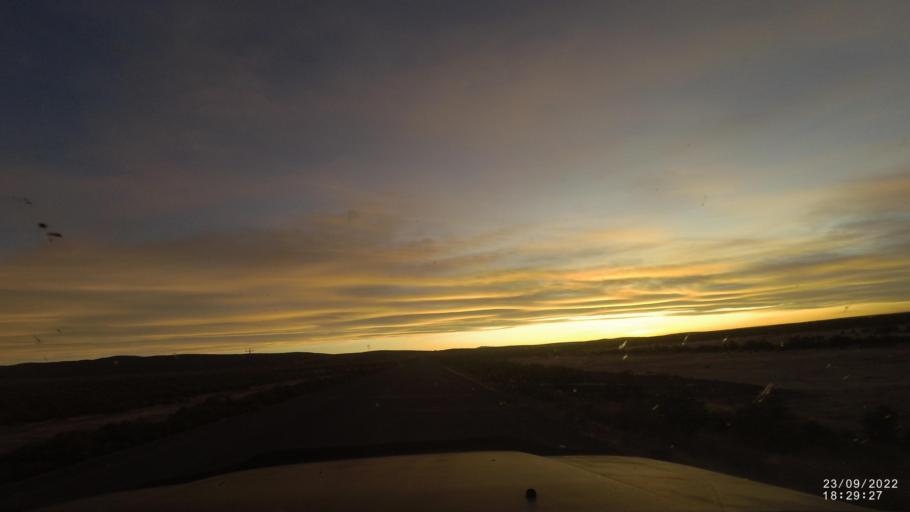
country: BO
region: Oruro
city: Challapata
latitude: -19.3452
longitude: -67.1922
